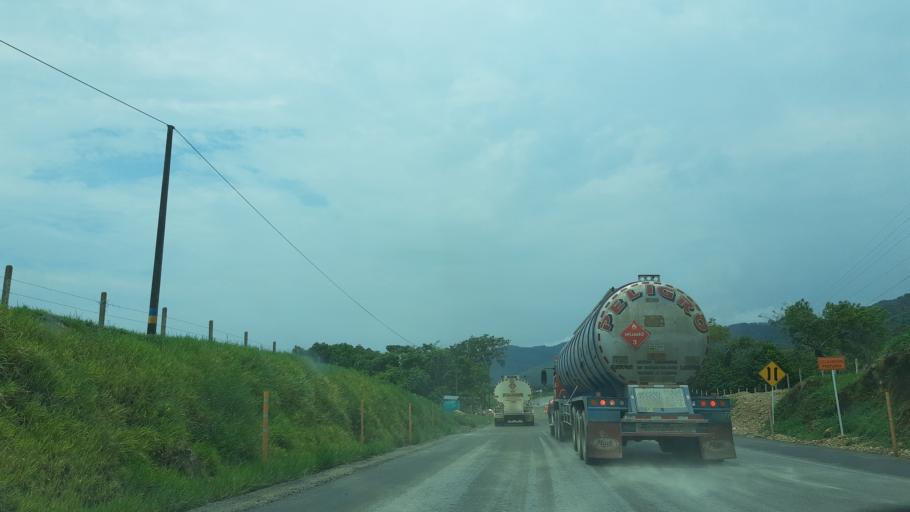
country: CO
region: Casanare
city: Sabanalarga
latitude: 4.7877
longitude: -72.9950
